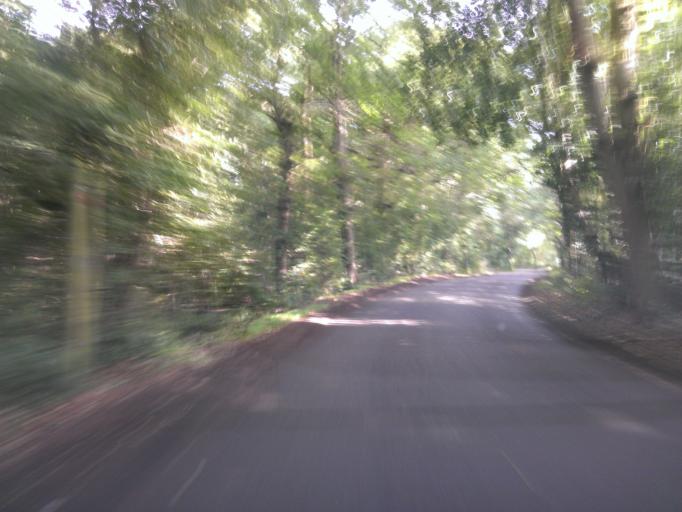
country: GB
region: England
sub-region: Essex
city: Saint Osyth
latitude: 51.8336
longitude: 1.1034
